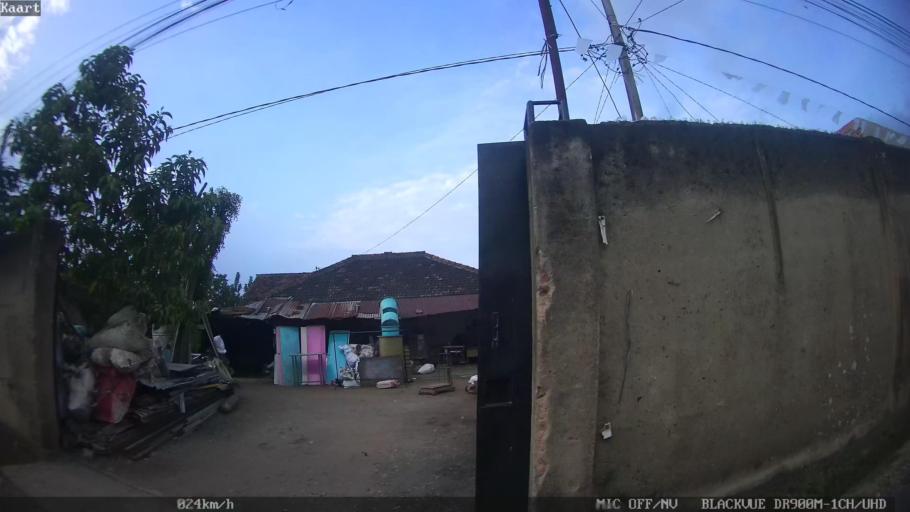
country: ID
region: Lampung
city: Bandarlampung
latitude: -5.4063
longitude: 105.3039
